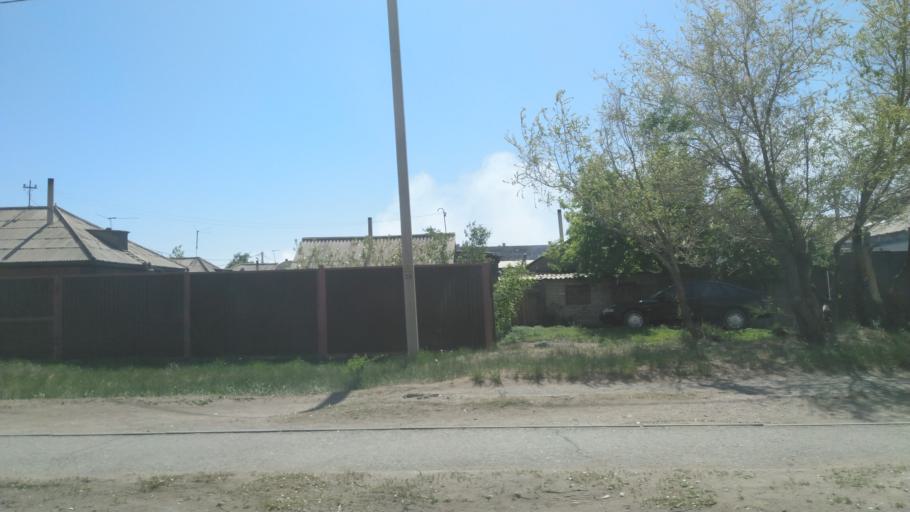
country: KZ
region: Pavlodar
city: Pavlodar
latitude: 52.2924
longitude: 77.0090
